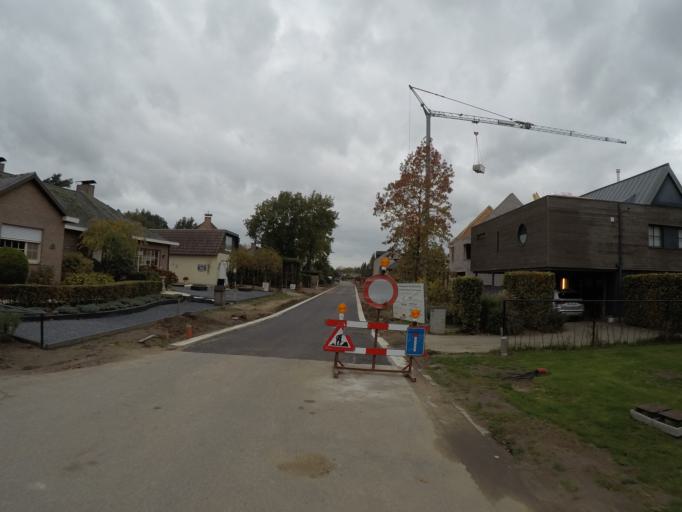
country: BE
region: Flanders
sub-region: Provincie Antwerpen
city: Zandhoven
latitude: 51.2417
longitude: 4.6408
